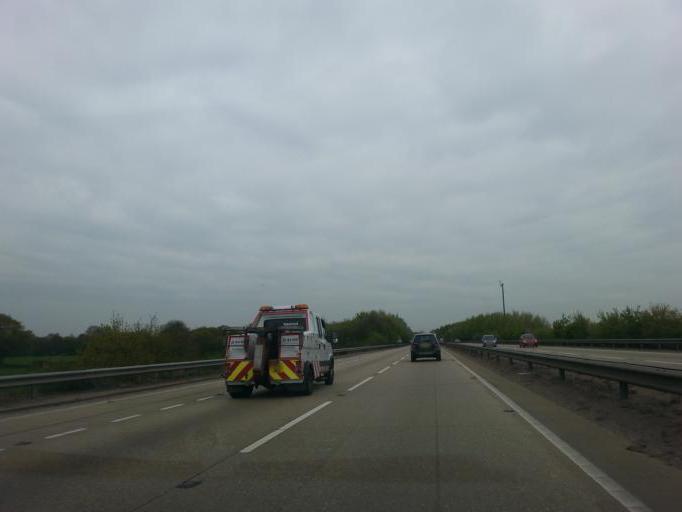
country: GB
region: England
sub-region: Suffolk
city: Bramford
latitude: 52.0686
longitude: 1.1103
